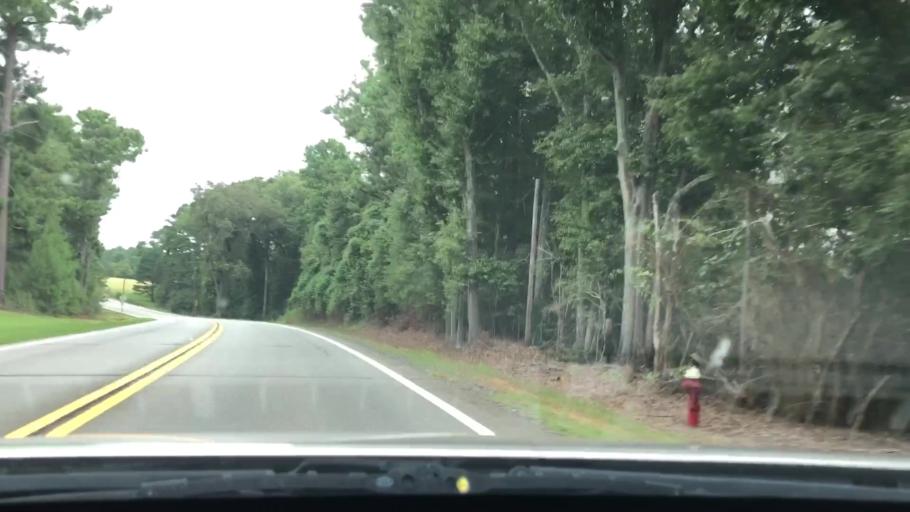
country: US
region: Georgia
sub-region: Upson County
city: Hannahs Mill
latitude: 33.0162
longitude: -84.4980
